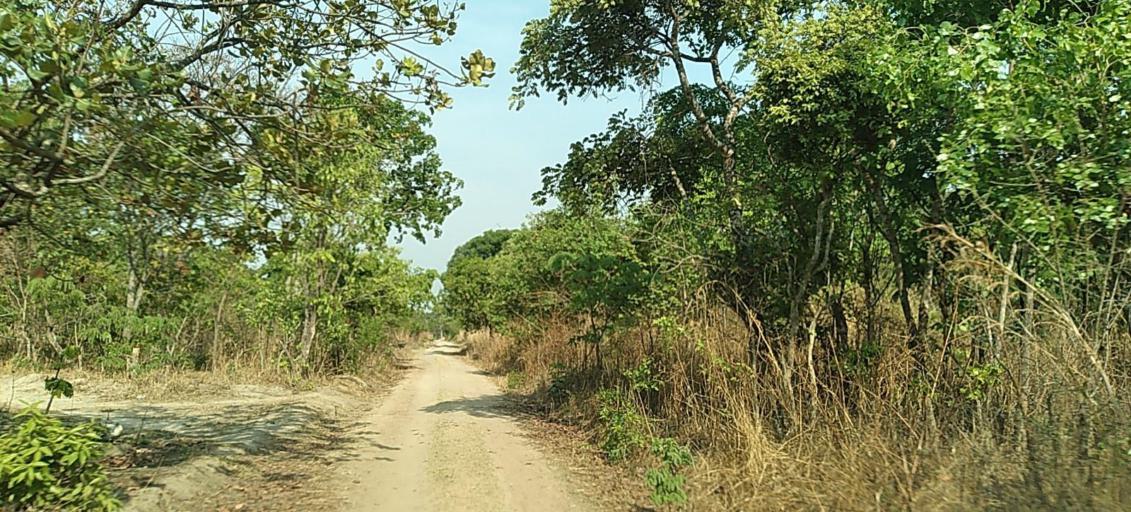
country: ZM
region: Copperbelt
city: Luanshya
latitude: -13.2185
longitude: 28.6560
